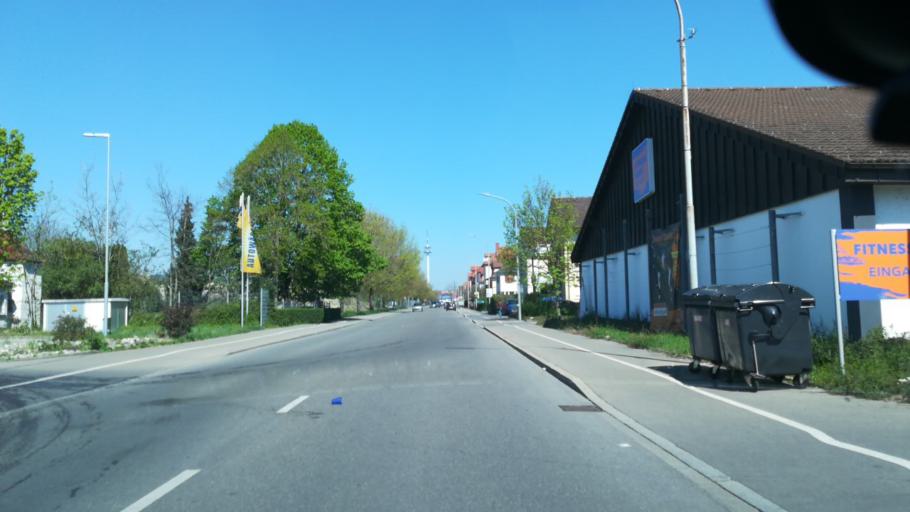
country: DE
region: Baden-Wuerttemberg
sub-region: Freiburg Region
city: Singen
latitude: 47.7553
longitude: 8.8521
